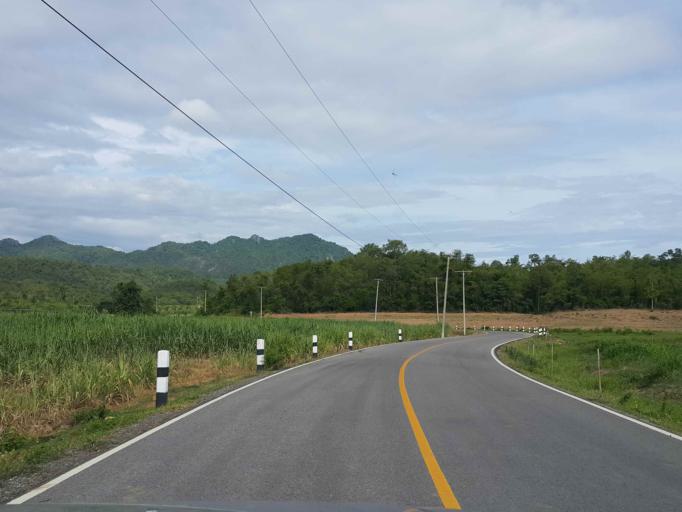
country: TH
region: Sukhothai
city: Thung Saliam
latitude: 17.2377
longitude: 99.5045
